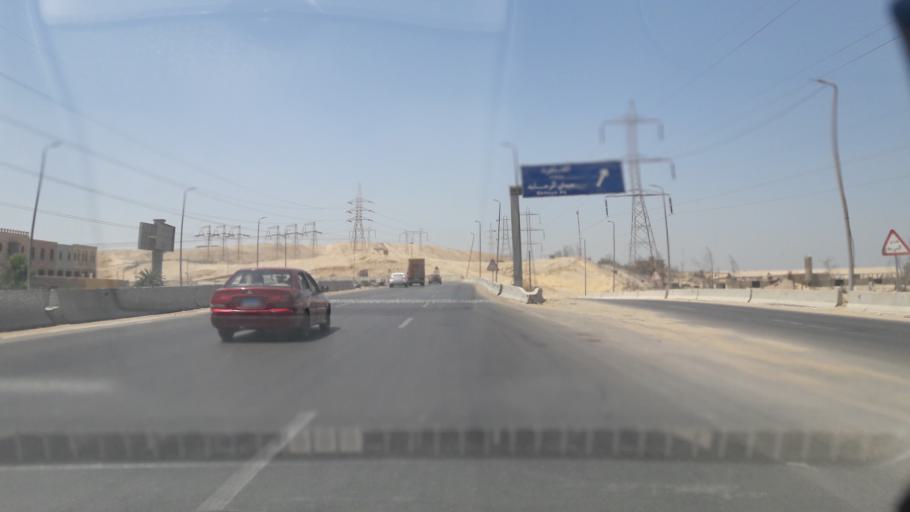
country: EG
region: Al Jizah
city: Awsim
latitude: 30.0217
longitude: 31.0815
